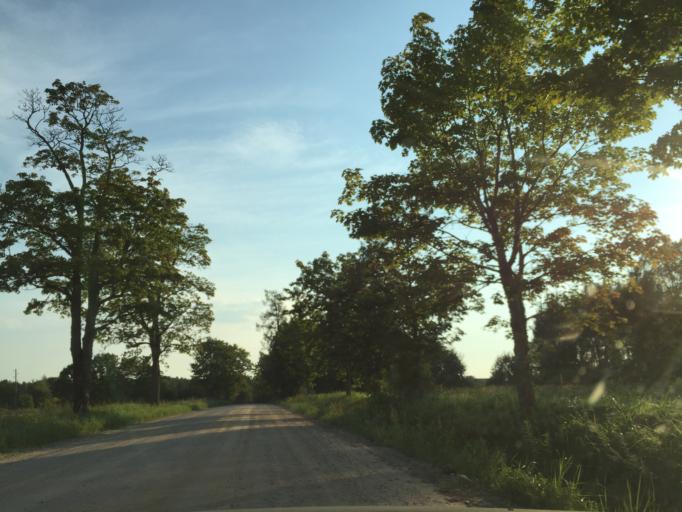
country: LV
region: Limbazu Rajons
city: Limbazi
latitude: 57.5537
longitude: 24.8024
